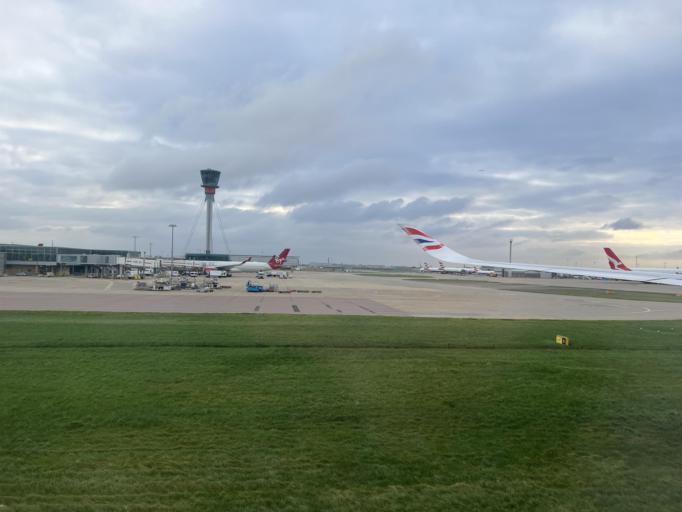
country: GB
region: England
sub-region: Greater London
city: West Drayton
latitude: 51.4759
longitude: -0.4663
